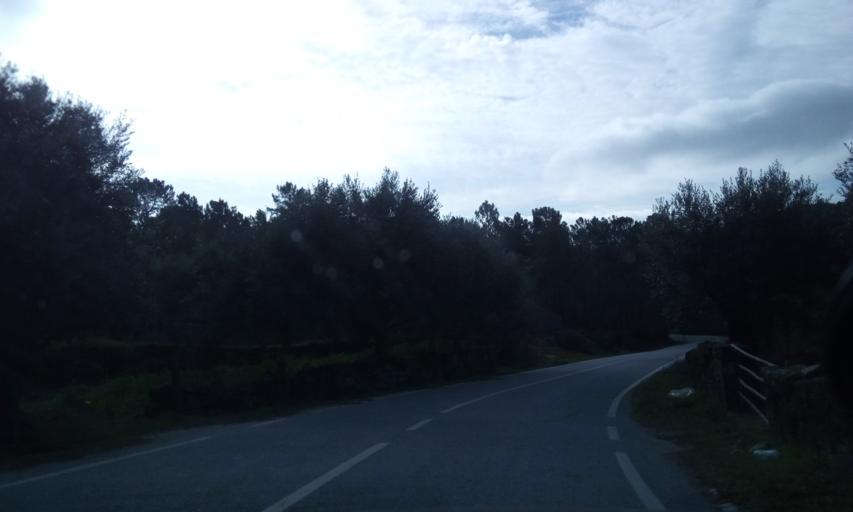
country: PT
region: Guarda
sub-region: Aguiar da Beira
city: Aguiar da Beira
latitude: 40.7269
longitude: -7.5598
